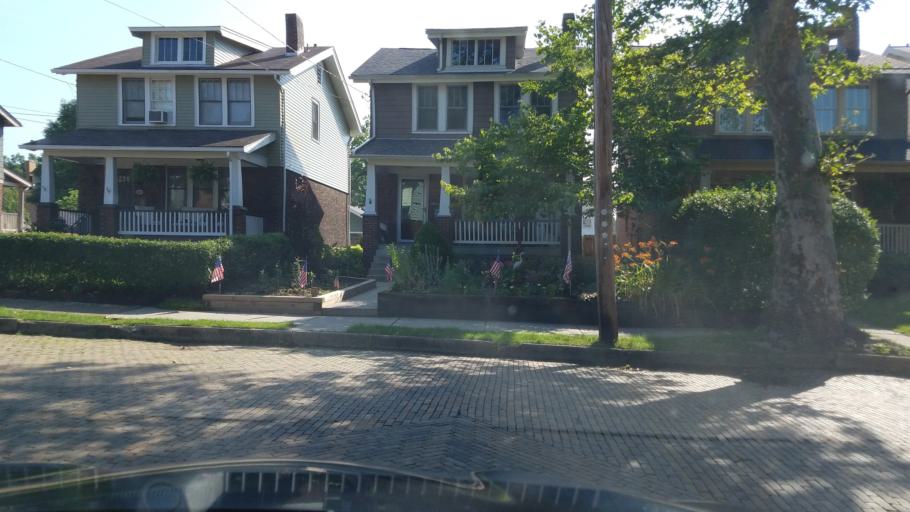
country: US
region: Pennsylvania
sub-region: Allegheny County
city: Edgewood
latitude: 40.4326
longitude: -79.8915
